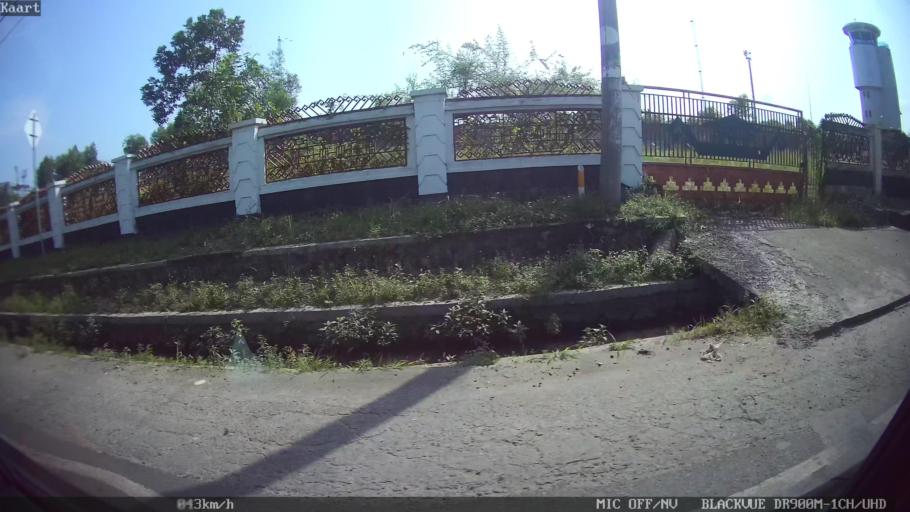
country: ID
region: Lampung
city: Natar
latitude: -5.2449
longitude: 105.1774
